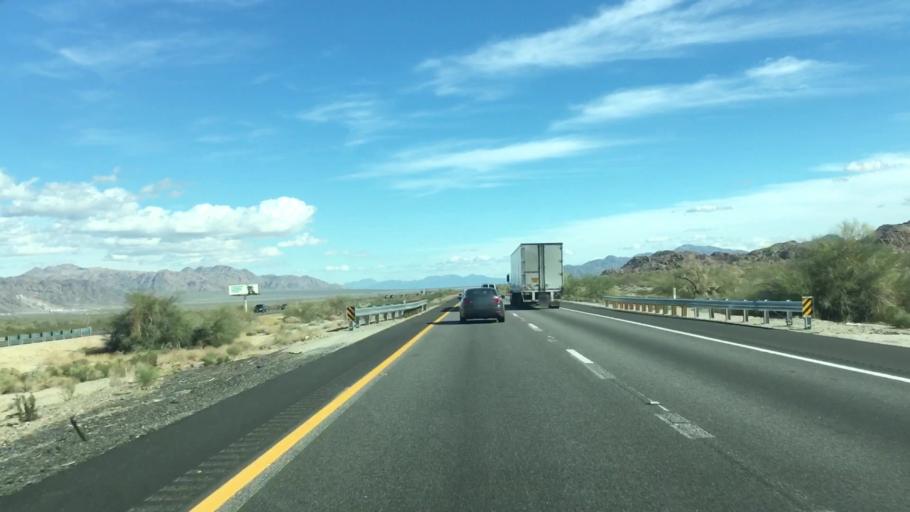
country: US
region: California
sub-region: Riverside County
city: Mecca
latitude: 33.6634
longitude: -115.6995
